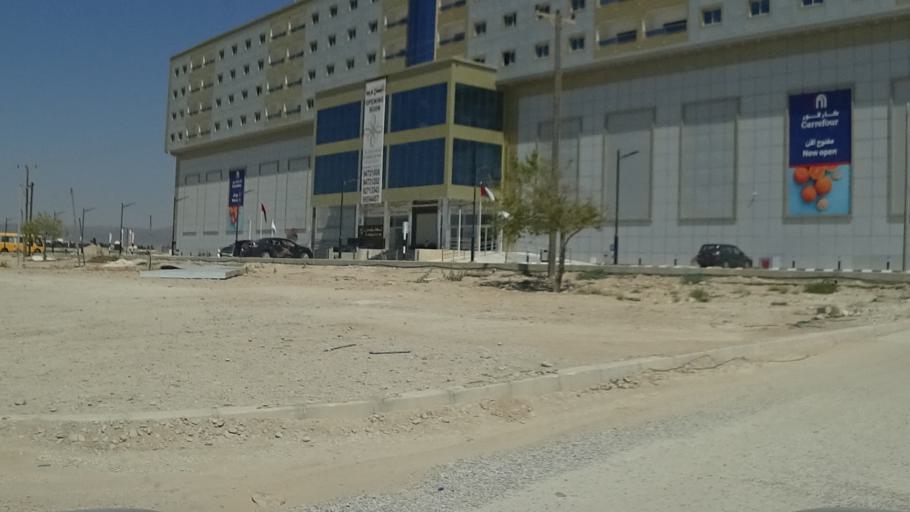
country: OM
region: Zufar
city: Salalah
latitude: 17.0513
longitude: 54.1672
